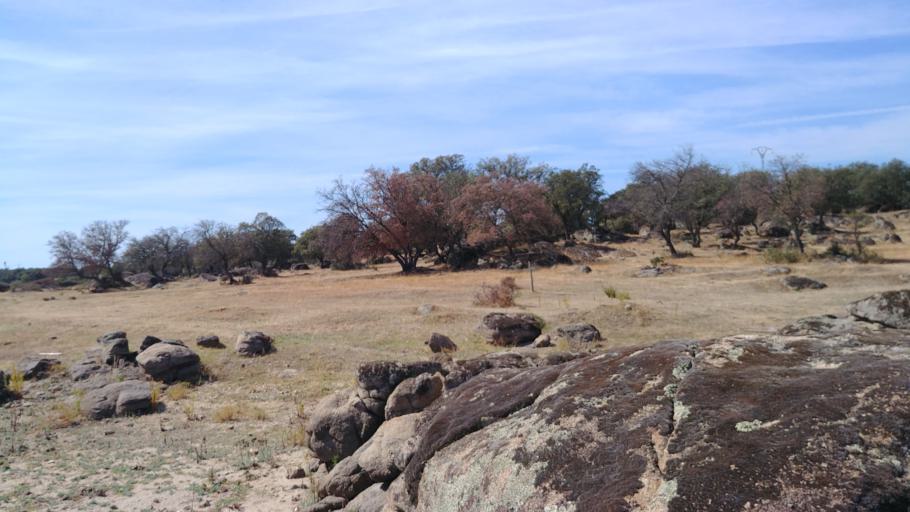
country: ES
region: Castille-La Mancha
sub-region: Province of Toledo
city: Navalcan
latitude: 40.0492
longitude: -5.1353
